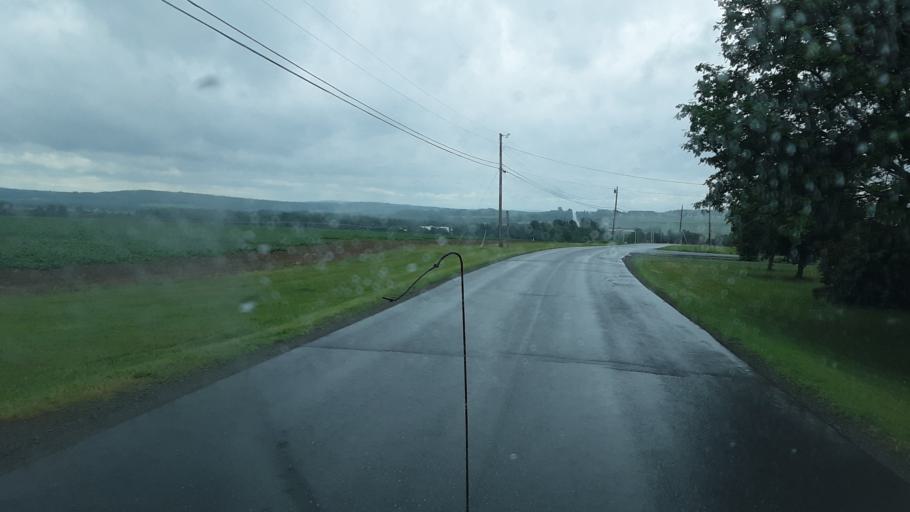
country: US
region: Maine
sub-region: Aroostook County
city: Presque Isle
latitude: 46.6819
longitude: -68.1744
